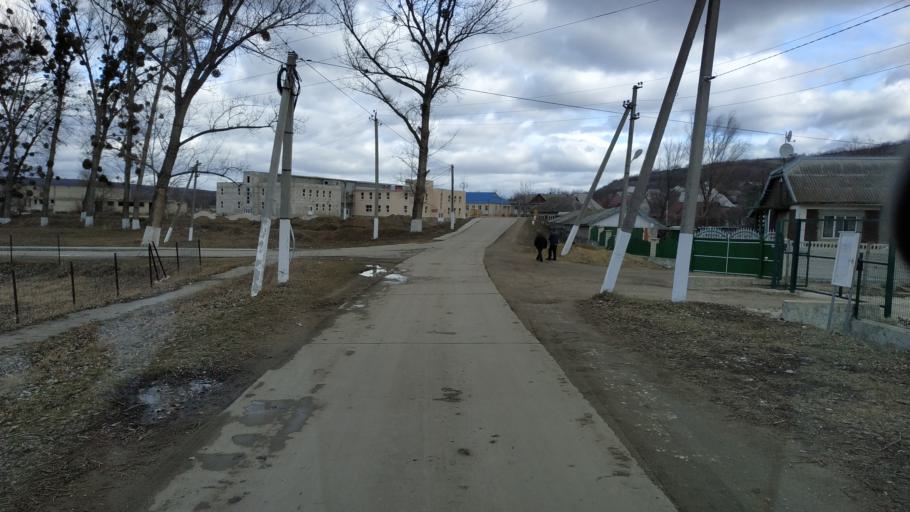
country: MD
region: Stinga Nistrului
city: Bucovat
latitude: 47.1334
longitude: 28.3857
